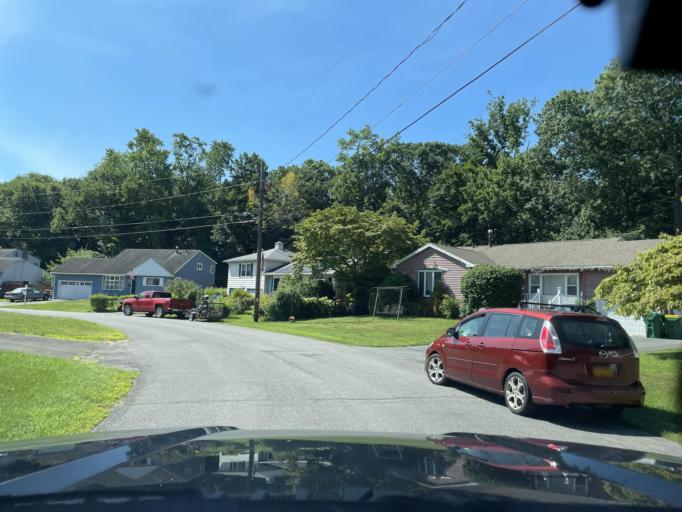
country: US
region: New York
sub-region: Ulster County
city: Saugerties South
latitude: 42.0640
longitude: -73.9611
